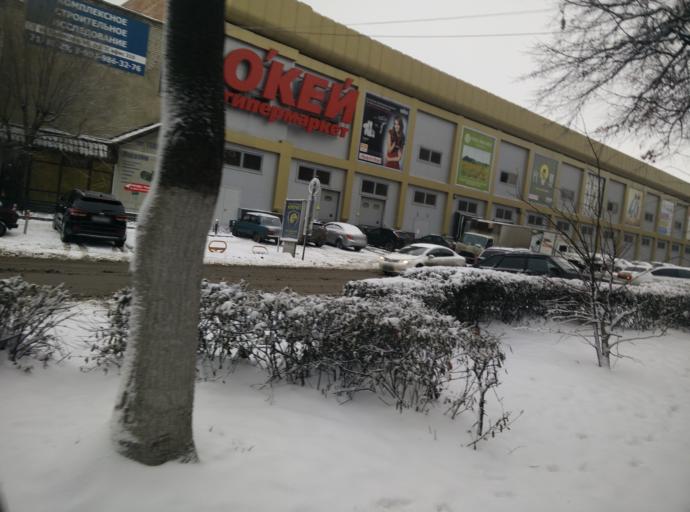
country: RU
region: Lipetsk
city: Lipetsk
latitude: 52.6068
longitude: 39.5795
